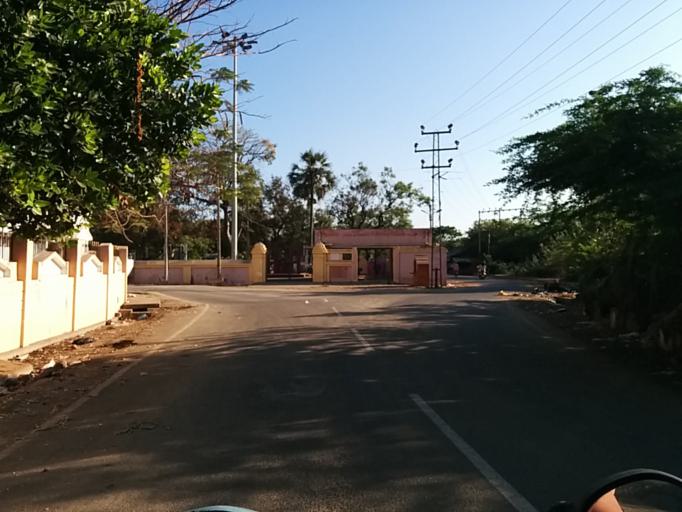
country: IN
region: Pondicherry
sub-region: Puducherry
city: Puducherry
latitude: 11.9189
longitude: 79.8299
